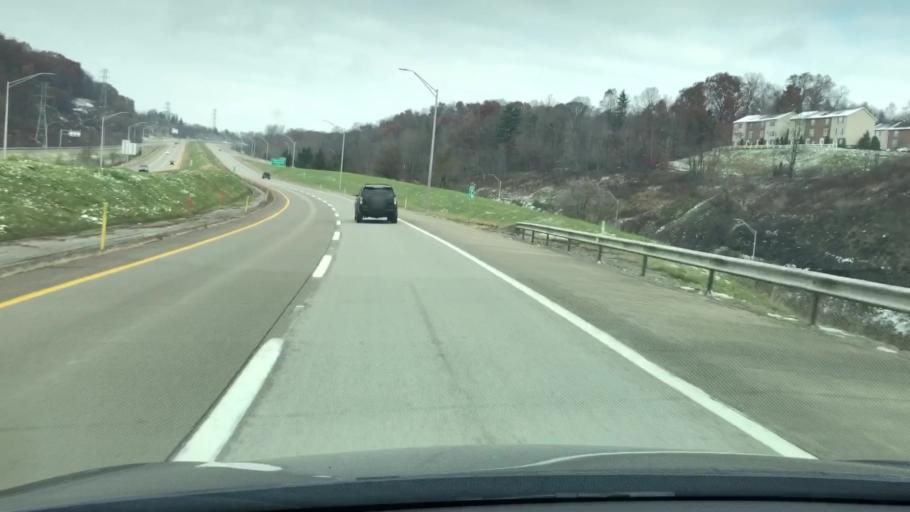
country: US
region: Pennsylvania
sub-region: Westmoreland County
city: Jeannette
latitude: 40.3266
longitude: -79.5796
